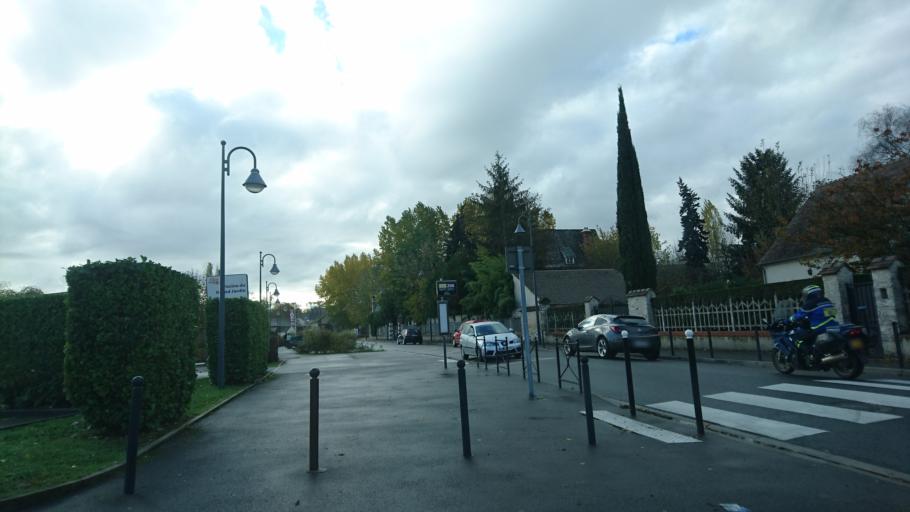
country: FR
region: Ile-de-France
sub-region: Departement de Seine-et-Marne
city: Moret-sur-Loing
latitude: 48.3751
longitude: 2.8202
